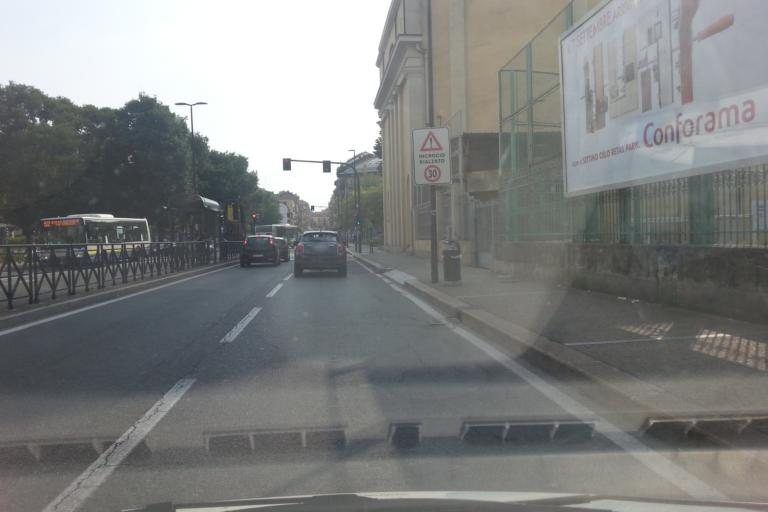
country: IT
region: Piedmont
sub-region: Provincia di Torino
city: Turin
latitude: 45.0857
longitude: 7.6688
